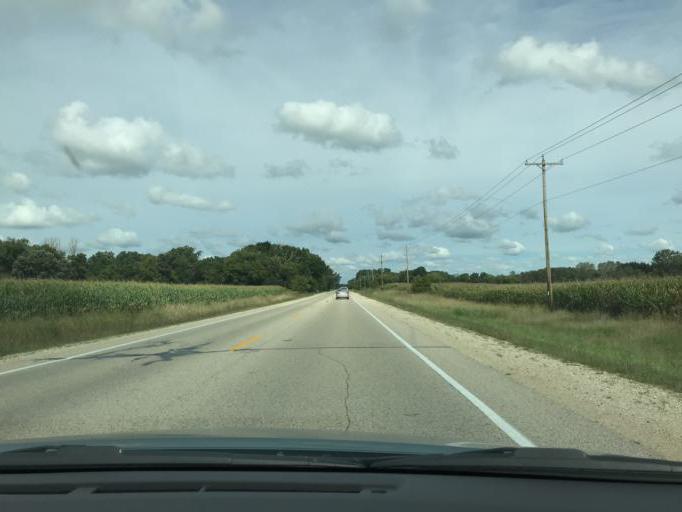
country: US
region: Wisconsin
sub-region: Racine County
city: Bohners Lake
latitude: 42.6167
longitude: -88.2346
